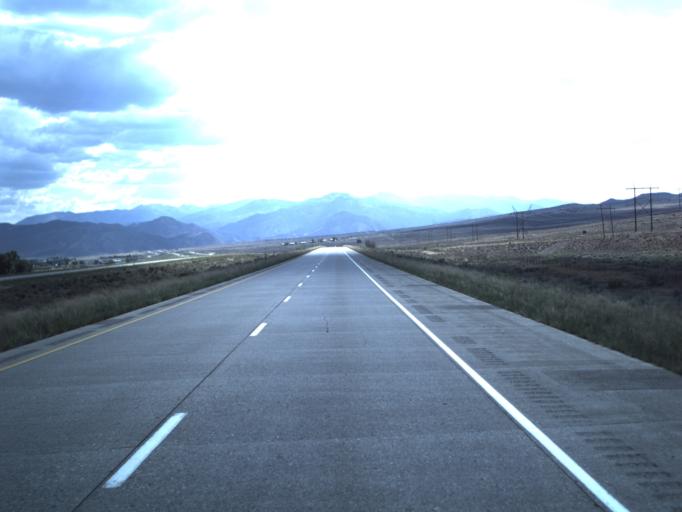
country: US
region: Utah
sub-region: Sevier County
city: Monroe
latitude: 38.6497
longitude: -112.2140
